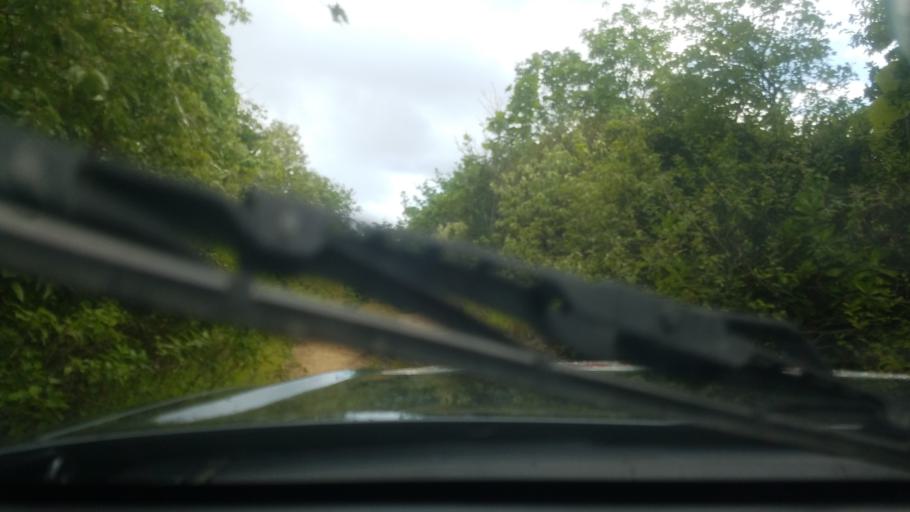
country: LC
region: Praslin
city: Praslin
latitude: 13.8675
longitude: -60.8911
